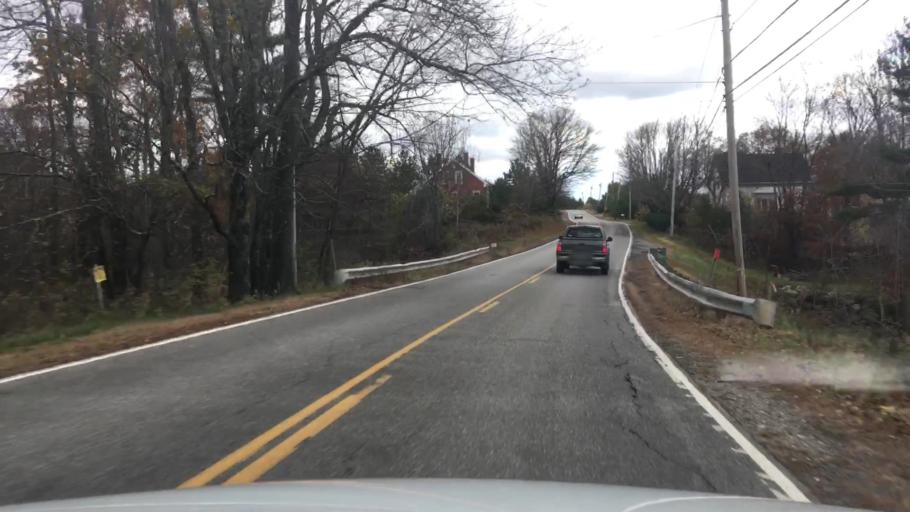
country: US
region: Maine
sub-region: Sagadahoc County
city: Richmond
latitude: 44.1148
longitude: -69.9096
